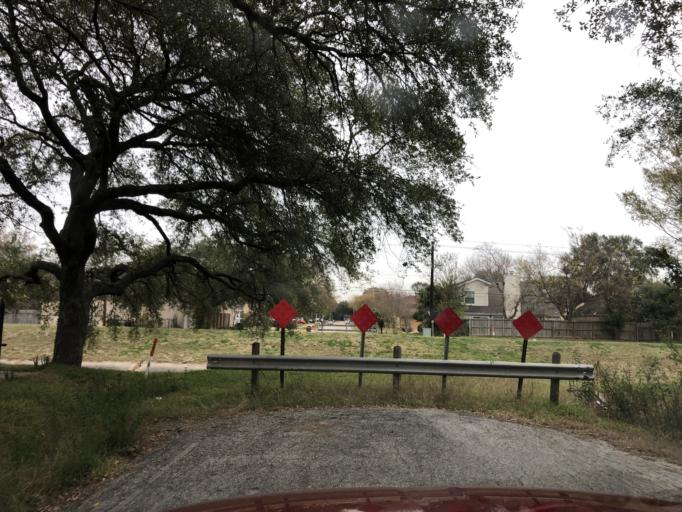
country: US
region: Texas
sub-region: Fort Bend County
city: Missouri City
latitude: 29.6378
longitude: -95.5252
